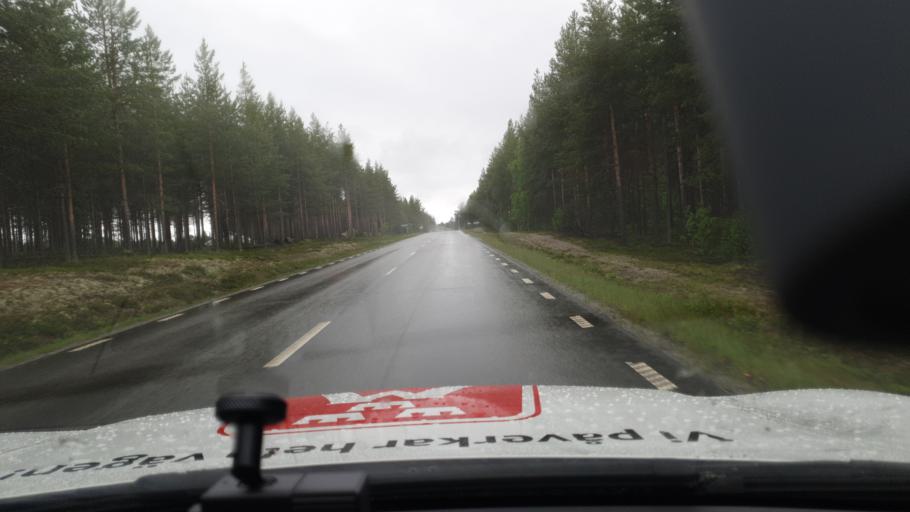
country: SE
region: Vaesterbotten
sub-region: Lycksele Kommun
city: Lycksele
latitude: 64.5723
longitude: 18.7140
